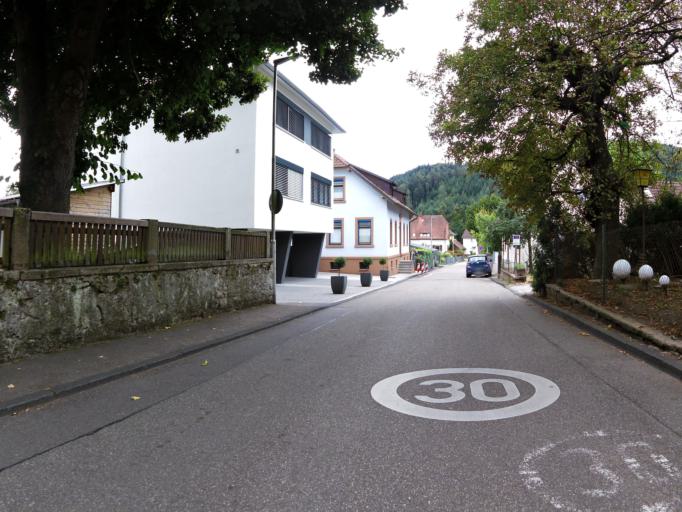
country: DE
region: Baden-Wuerttemberg
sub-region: Freiburg Region
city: Hohberg
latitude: 48.3385
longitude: 7.9087
